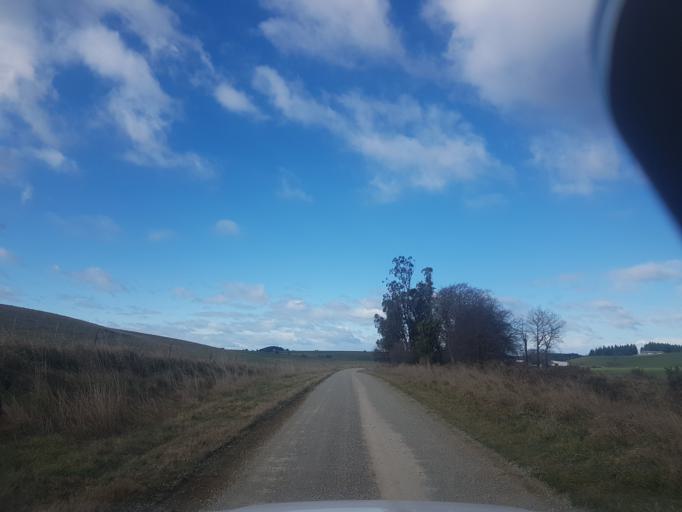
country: NZ
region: Canterbury
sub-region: Timaru District
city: Pleasant Point
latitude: -44.1874
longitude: 171.1910
